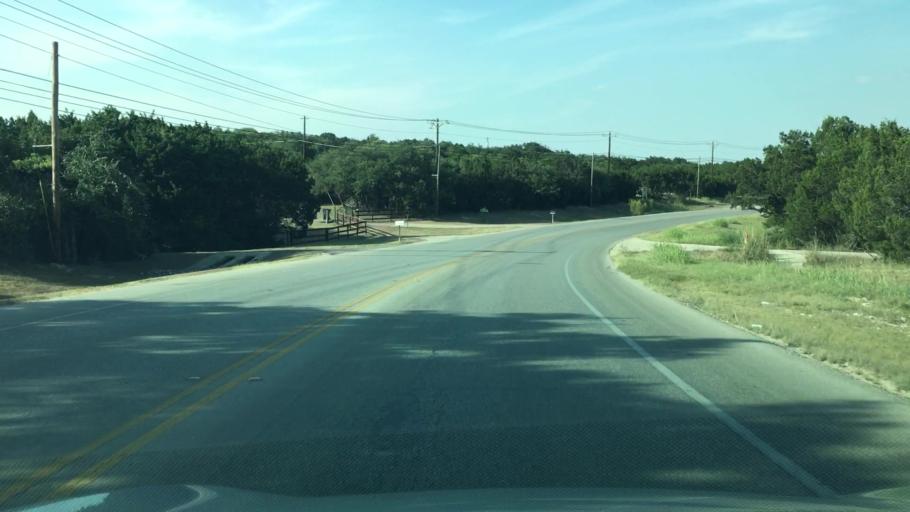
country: US
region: Texas
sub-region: Hays County
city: Dripping Springs
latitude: 30.1898
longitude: -98.0002
